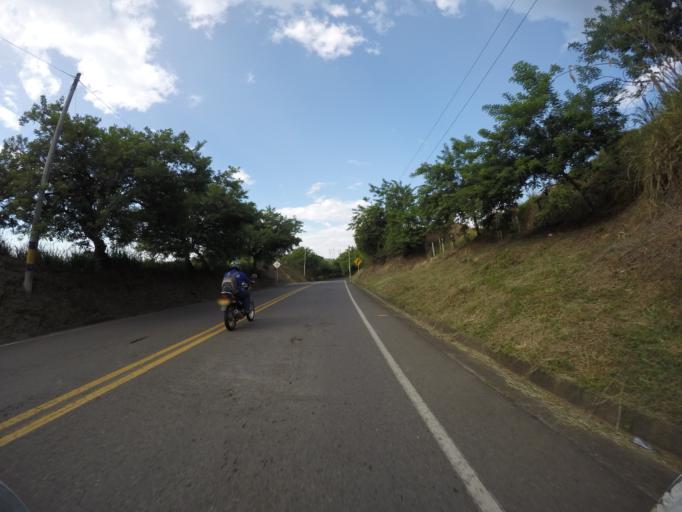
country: CO
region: Valle del Cauca
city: Cartago
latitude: 4.7250
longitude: -75.8817
